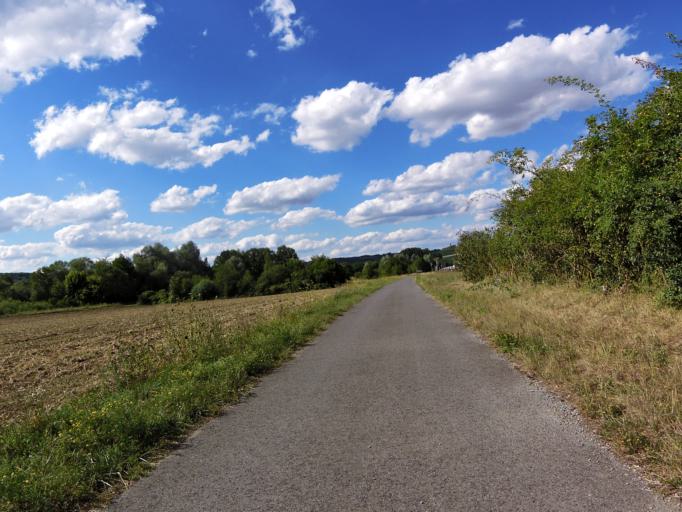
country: DE
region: Bavaria
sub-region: Regierungsbezirk Unterfranken
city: Eibelstadt
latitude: 49.7404
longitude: 9.9892
